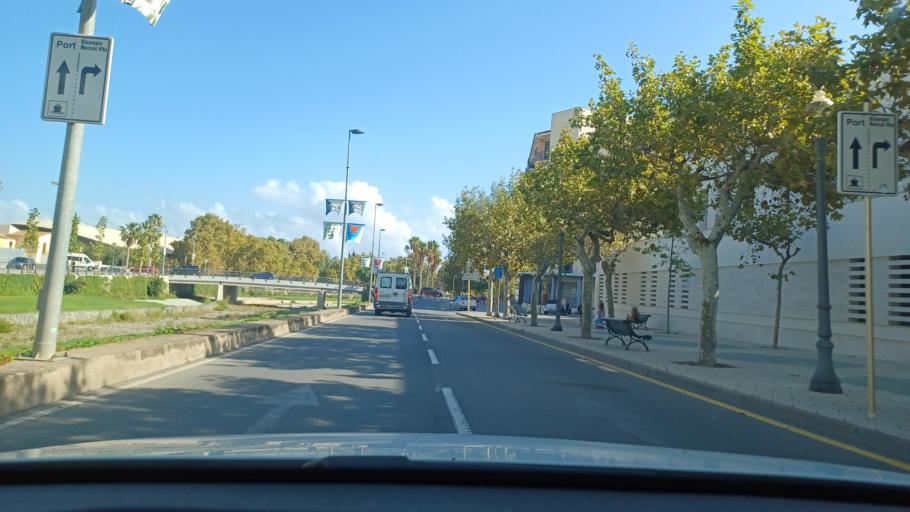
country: ES
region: Catalonia
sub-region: Provincia de Tarragona
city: Cambrils
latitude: 41.0735
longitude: 1.0547
